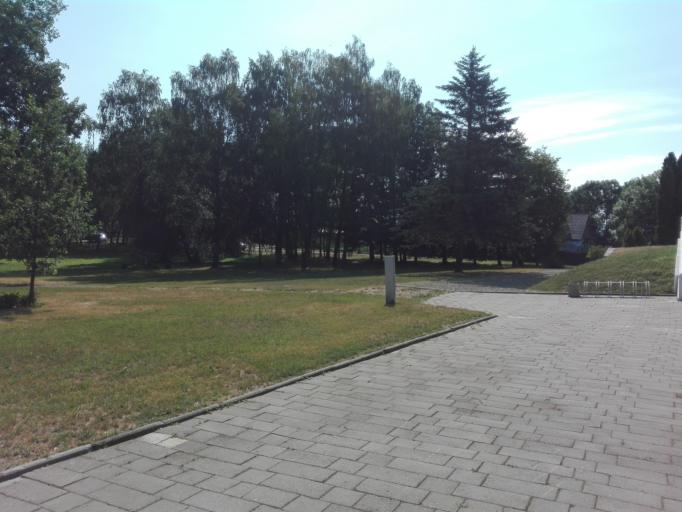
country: LT
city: Grigiskes
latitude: 54.8680
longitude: 25.0615
